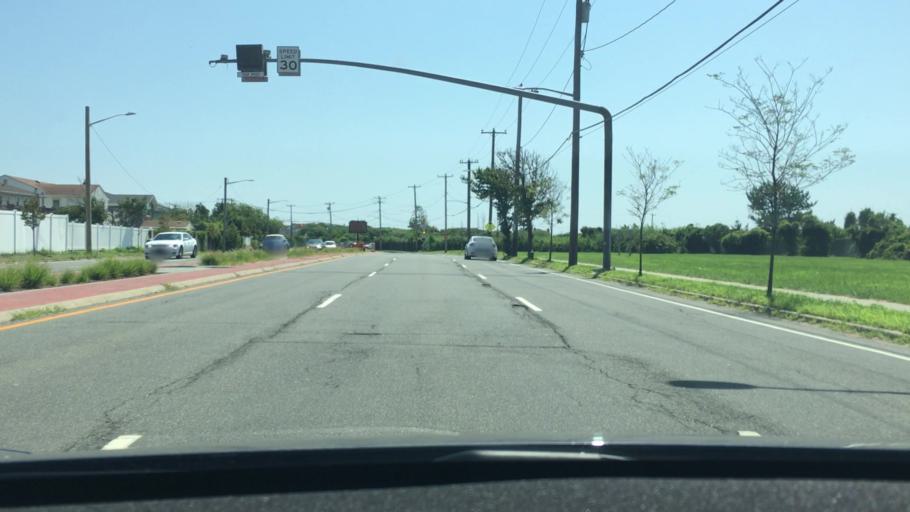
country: US
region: New York
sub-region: Nassau County
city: Lido Beach
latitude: 40.5881
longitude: -73.6324
